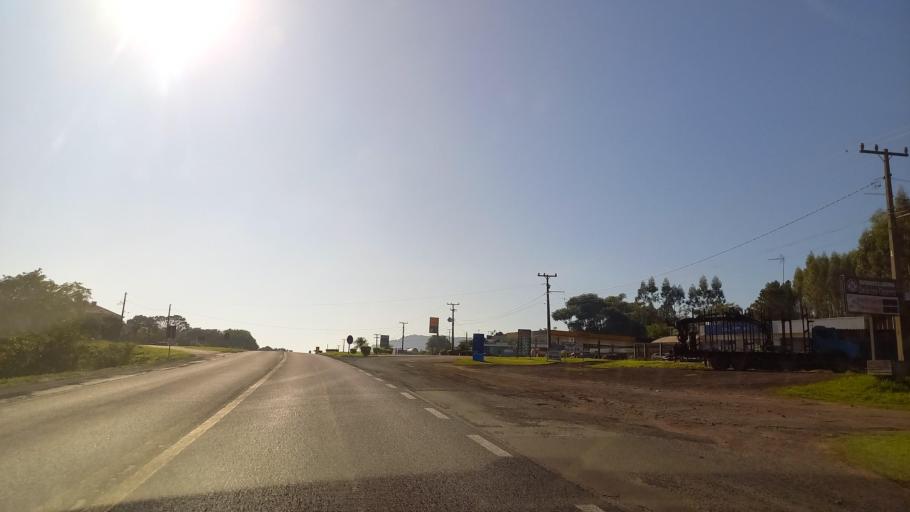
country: BR
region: Rio Grande do Sul
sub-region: Taquari
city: Taquari
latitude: -29.7102
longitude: -51.7670
